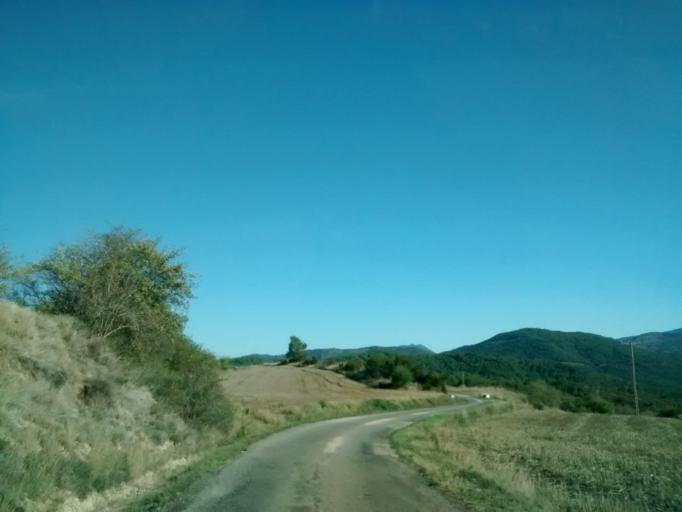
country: ES
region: Aragon
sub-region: Provincia de Huesca
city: Santa Cruz de la Seros
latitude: 42.4374
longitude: -0.6597
